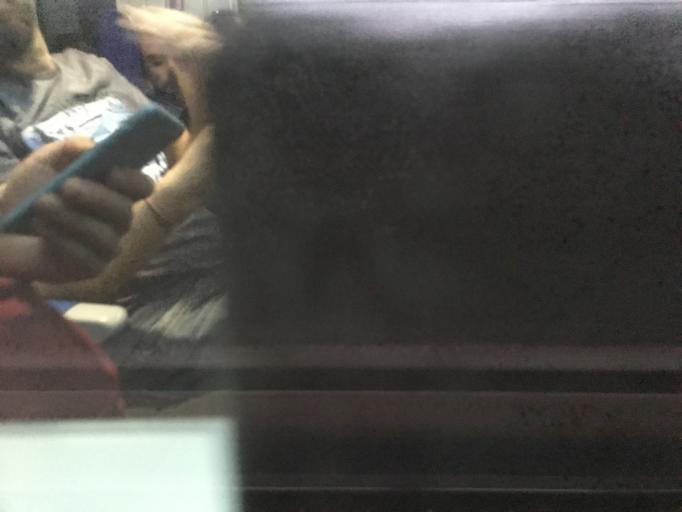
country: TR
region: Kocaeli
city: Derince
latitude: 40.7490
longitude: 29.8001
